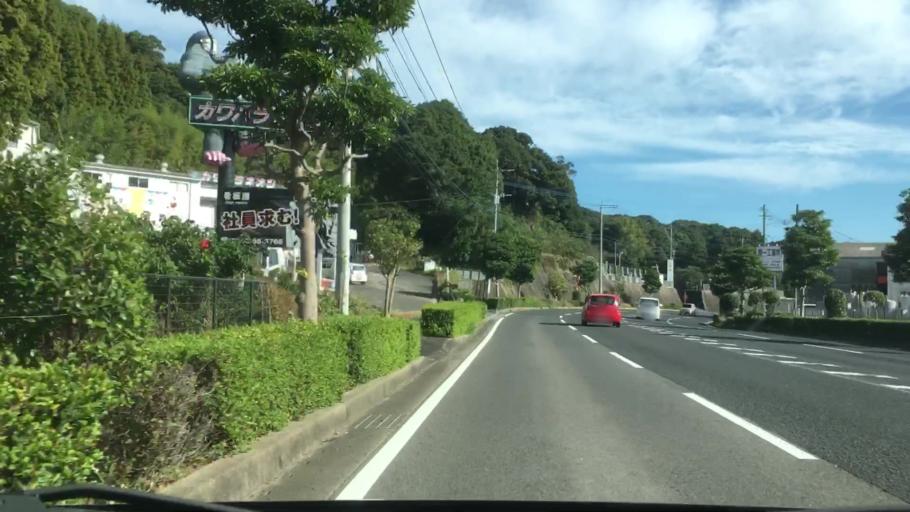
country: JP
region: Nagasaki
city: Sasebo
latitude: 33.1125
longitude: 129.7872
